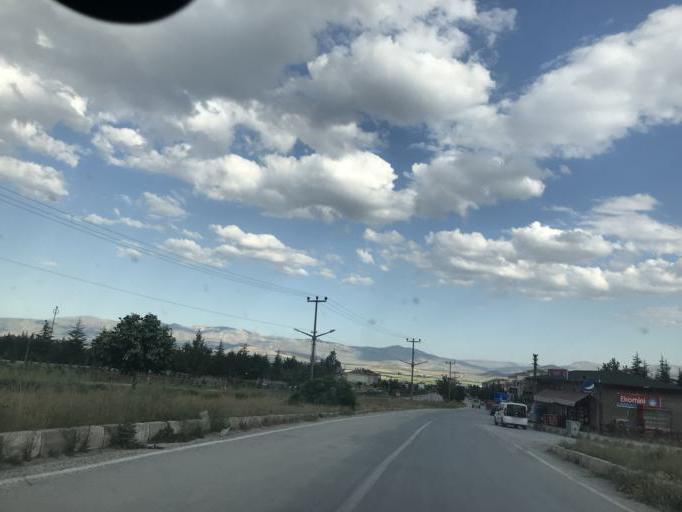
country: TR
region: Burdur
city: Karamanli
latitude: 37.3804
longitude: 29.8276
